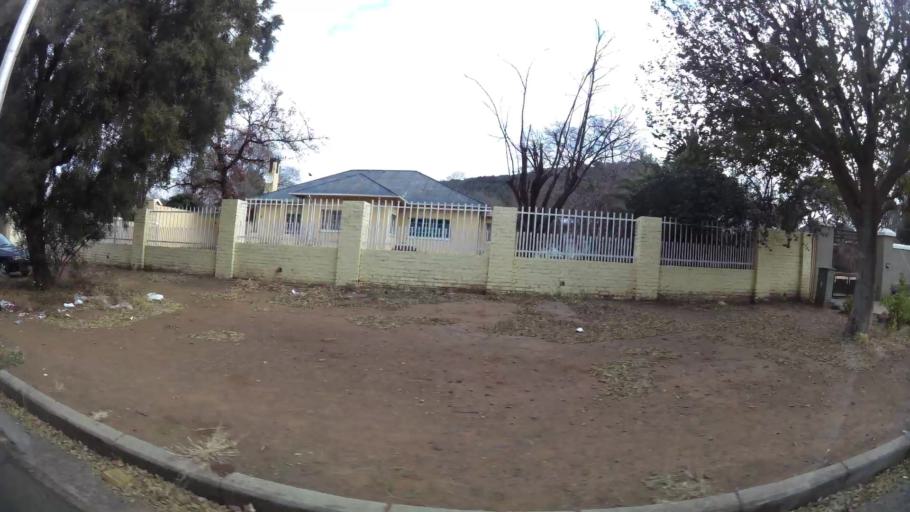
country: ZA
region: Orange Free State
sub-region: Mangaung Metropolitan Municipality
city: Bloemfontein
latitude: -29.0949
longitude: 26.2451
